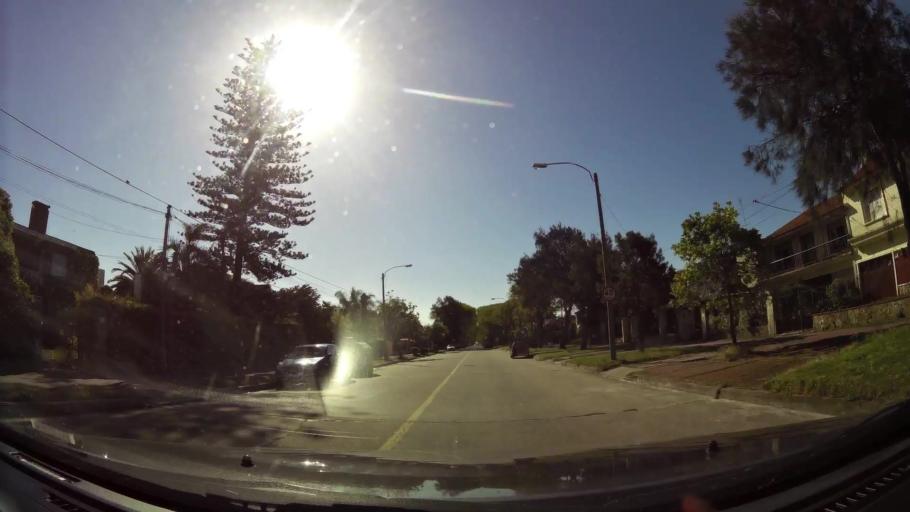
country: UY
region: Canelones
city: Paso de Carrasco
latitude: -34.8950
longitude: -56.0608
